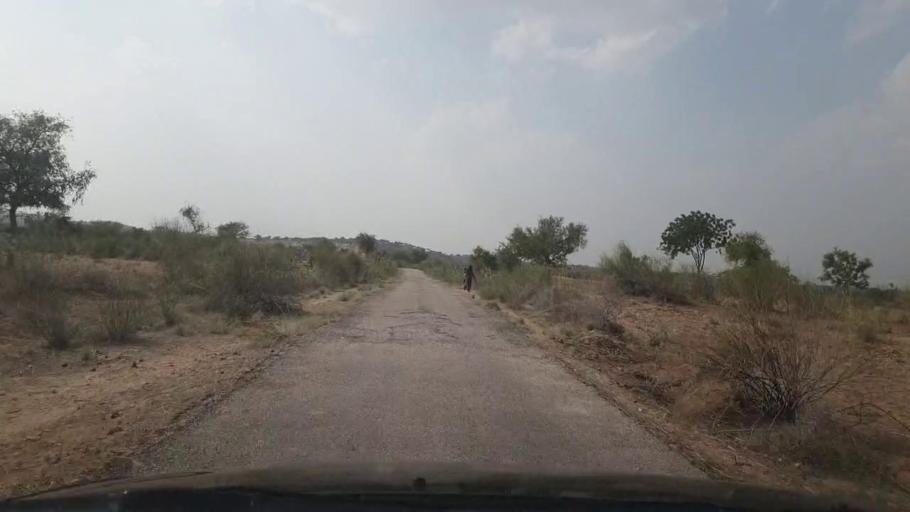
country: PK
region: Sindh
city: Islamkot
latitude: 24.9660
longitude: 70.6206
